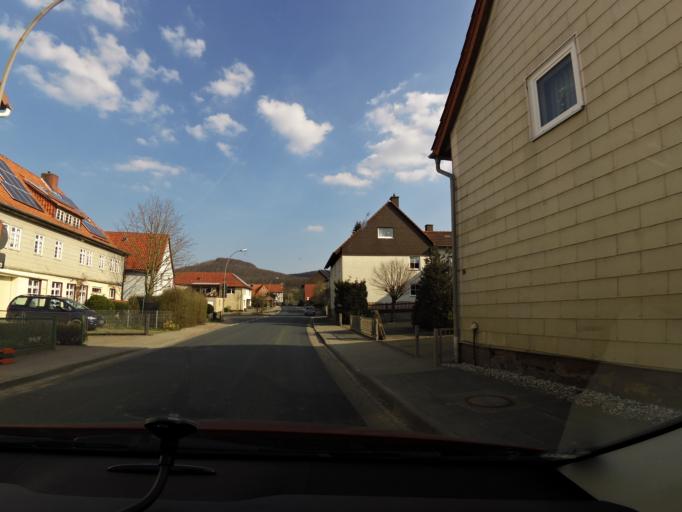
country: DE
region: Lower Saxony
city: Waake
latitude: 51.5972
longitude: 10.0229
